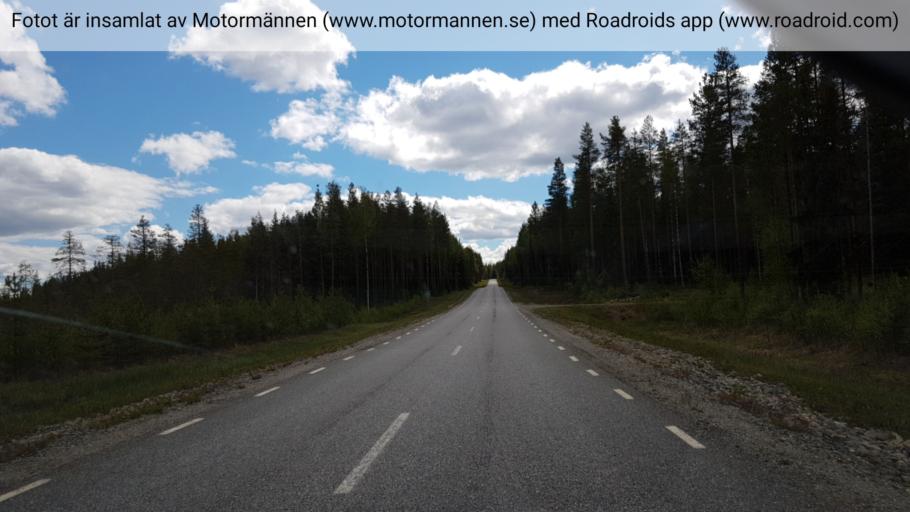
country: SE
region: Vaesterbotten
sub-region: Skelleftea Kommun
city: Langsele
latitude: 64.7060
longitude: 19.9896
